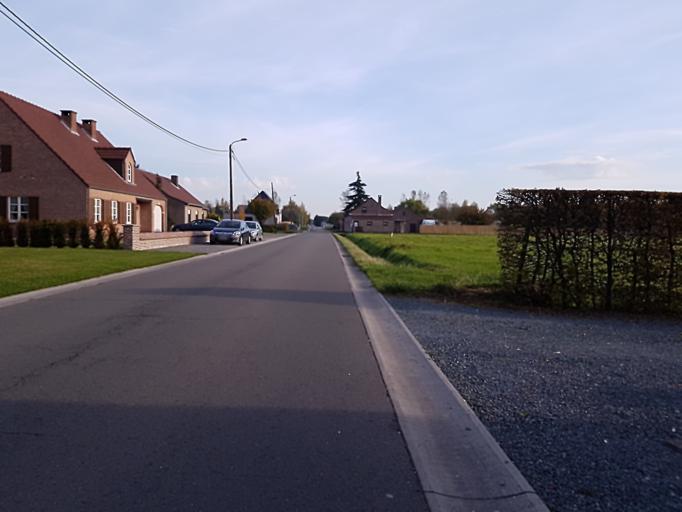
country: BE
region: Flanders
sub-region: Provincie Antwerpen
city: Sint-Katelijne-Waver
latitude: 51.0583
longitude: 4.4999
